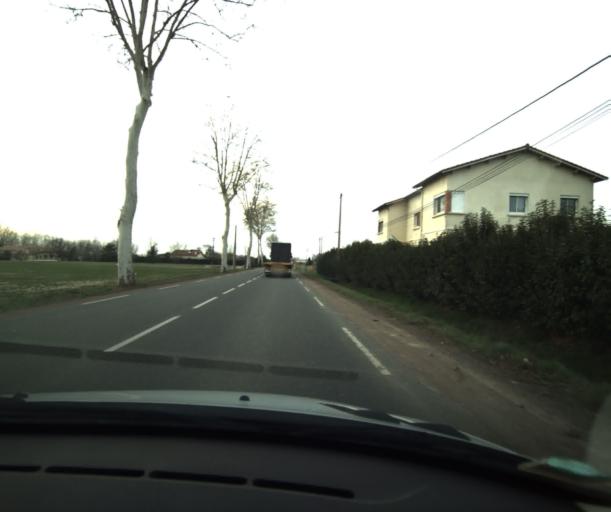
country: FR
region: Midi-Pyrenees
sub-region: Departement du Tarn-et-Garonne
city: Saint-Porquier
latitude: 44.0228
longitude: 1.1528
